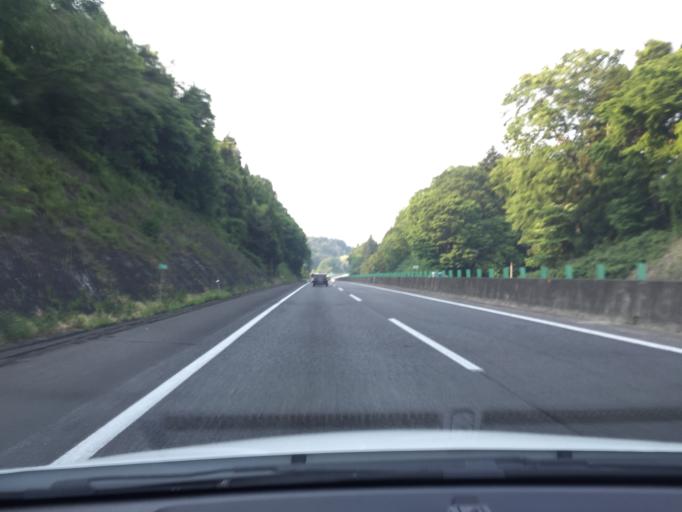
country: JP
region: Fukushima
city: Sukagawa
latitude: 37.1688
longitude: 140.2702
